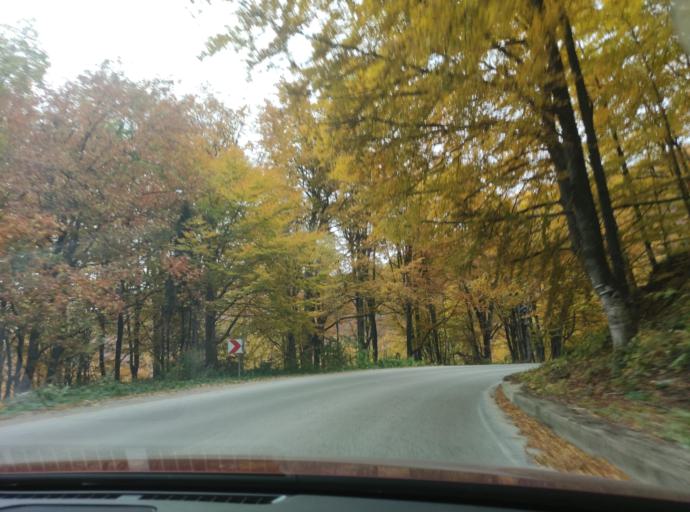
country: BG
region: Montana
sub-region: Obshtina Berkovitsa
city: Berkovitsa
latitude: 43.1324
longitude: 23.1429
